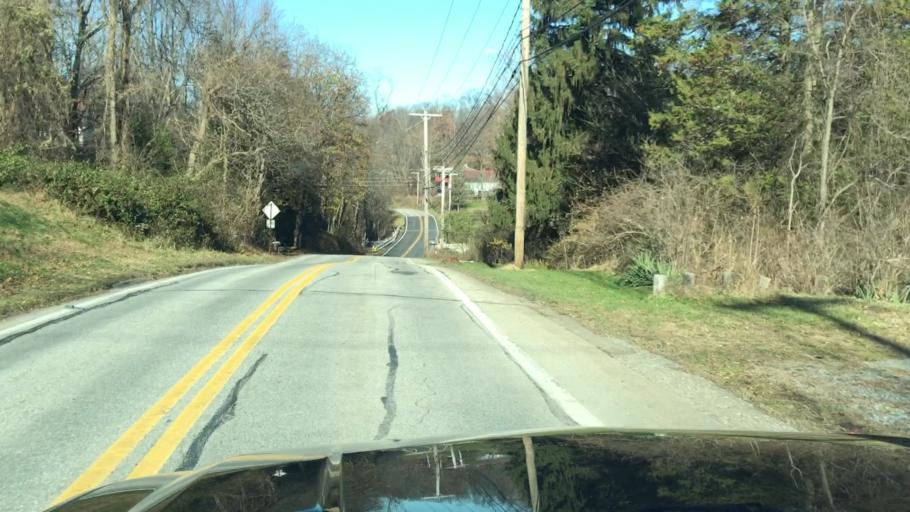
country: US
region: Pennsylvania
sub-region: Cumberland County
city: Lower Allen
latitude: 40.1827
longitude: -76.8829
